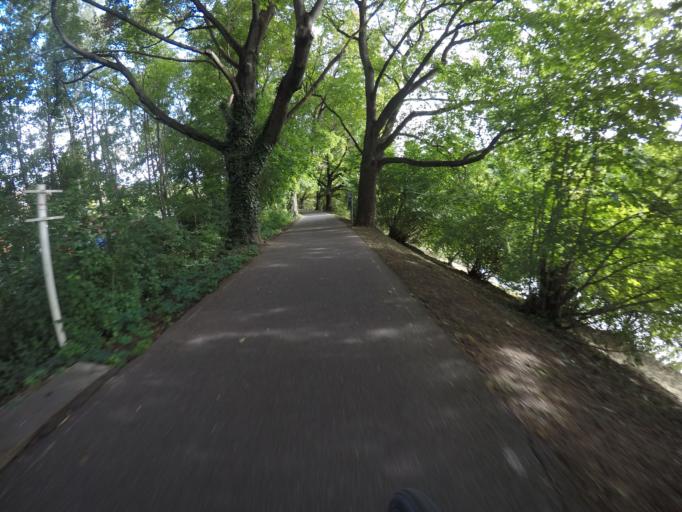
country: DE
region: Baden-Wuerttemberg
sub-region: Regierungsbezirk Stuttgart
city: Stuttgart Muehlhausen
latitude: 48.8177
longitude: 9.2266
